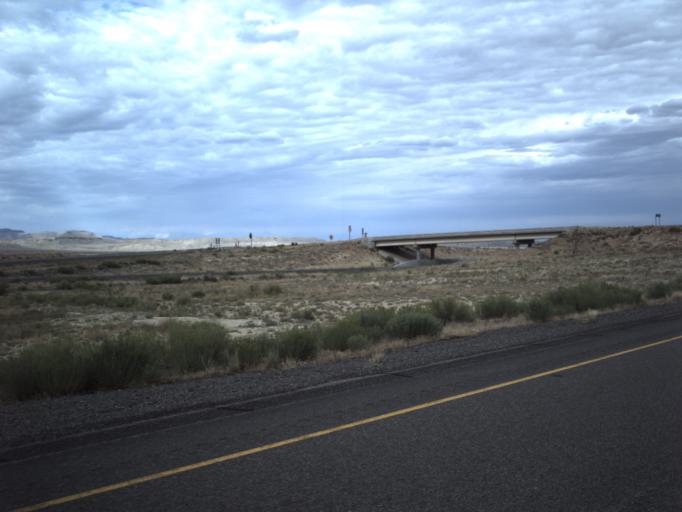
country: US
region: Utah
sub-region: Grand County
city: Moab
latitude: 38.9418
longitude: -109.6170
